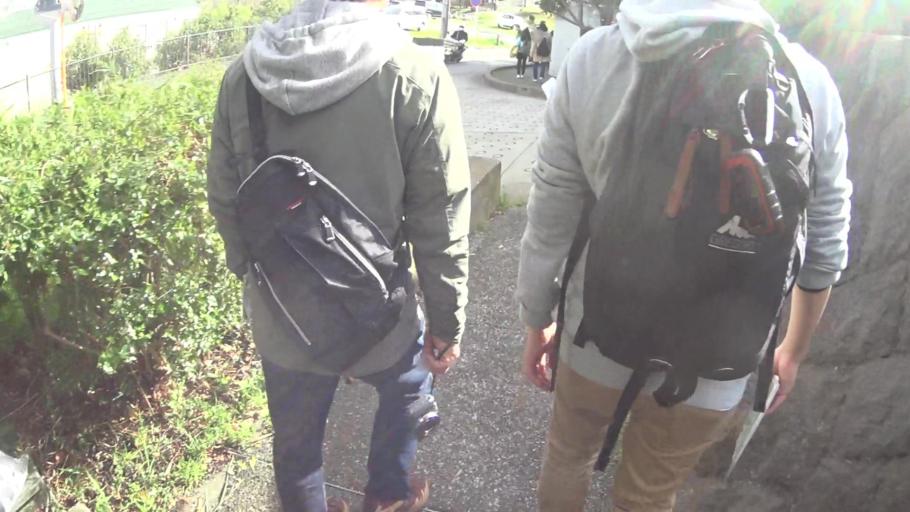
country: JP
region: Kanagawa
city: Kamakura
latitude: 35.3242
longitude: 139.5139
